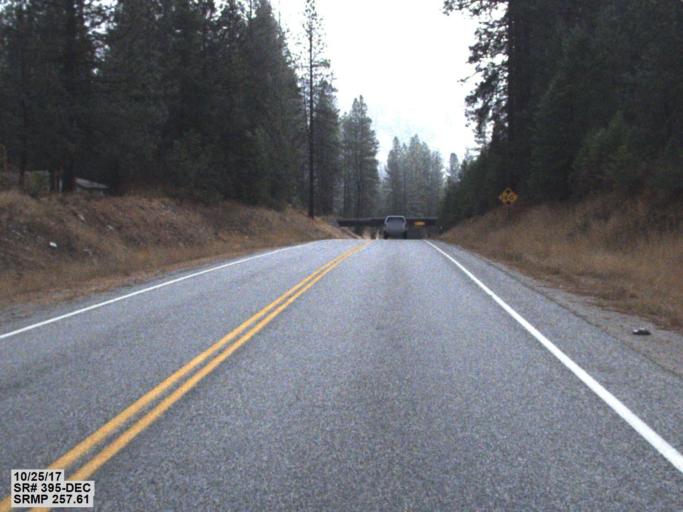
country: US
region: Washington
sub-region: Stevens County
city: Kettle Falls
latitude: 48.8353
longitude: -118.1829
